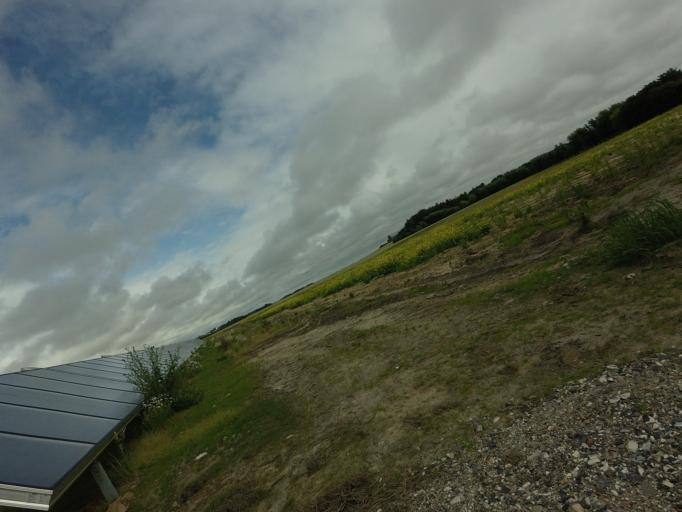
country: DK
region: North Denmark
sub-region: Jammerbugt Kommune
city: Pandrup
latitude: 57.3700
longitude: 9.7347
